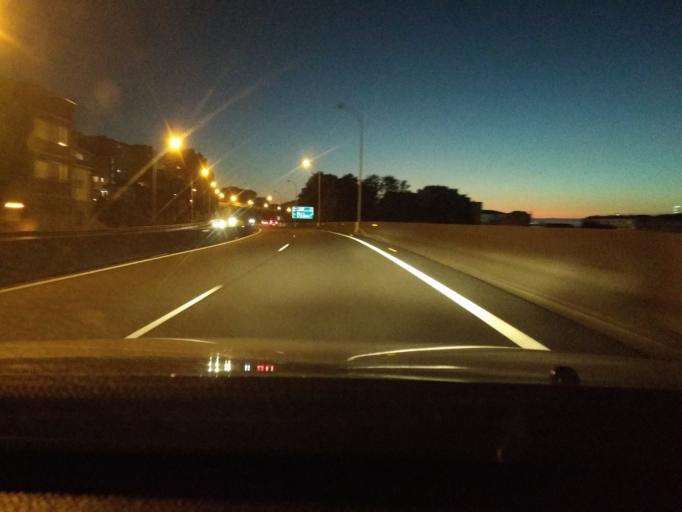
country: ES
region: Galicia
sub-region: Provincia de Pontevedra
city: Vigo
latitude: 42.2454
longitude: -8.6981
